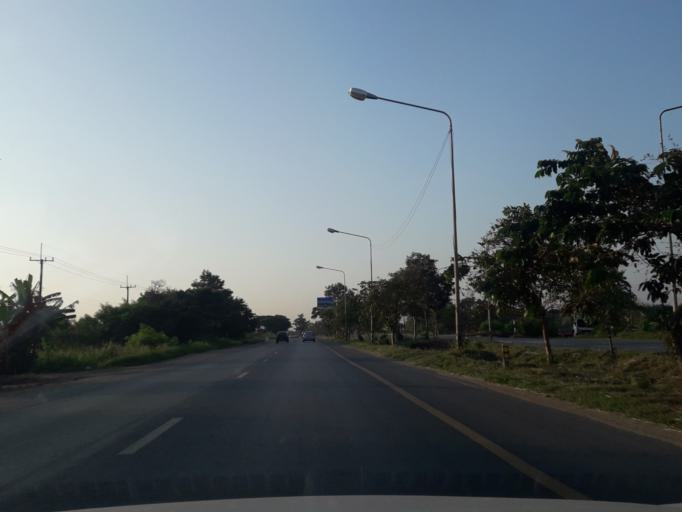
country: TH
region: Phra Nakhon Si Ayutthaya
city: Bang Pa-in
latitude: 14.2264
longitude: 100.5405
